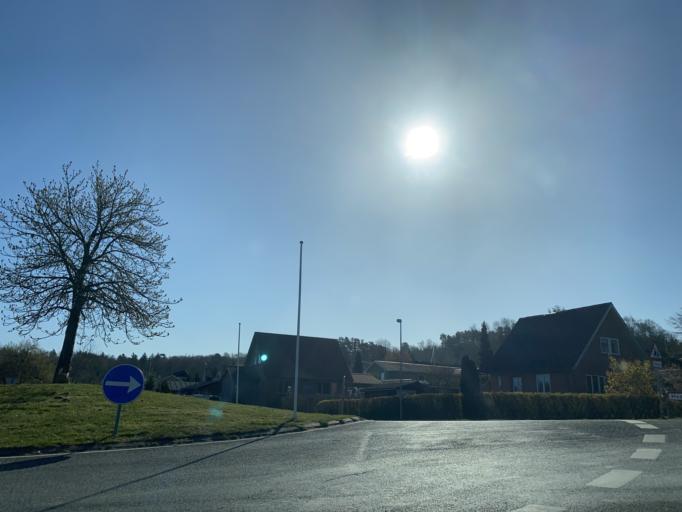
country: DK
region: Central Jutland
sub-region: Favrskov Kommune
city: Ulstrup
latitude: 56.3867
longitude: 9.7876
